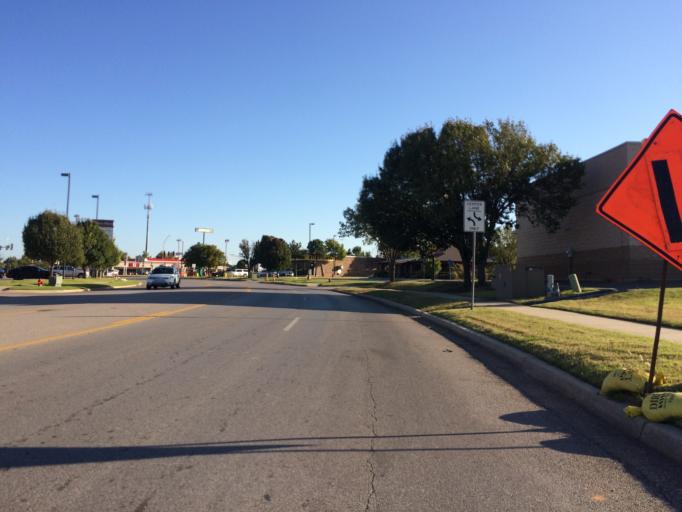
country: US
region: Oklahoma
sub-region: Cleveland County
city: Norman
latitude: 35.2315
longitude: -97.4899
